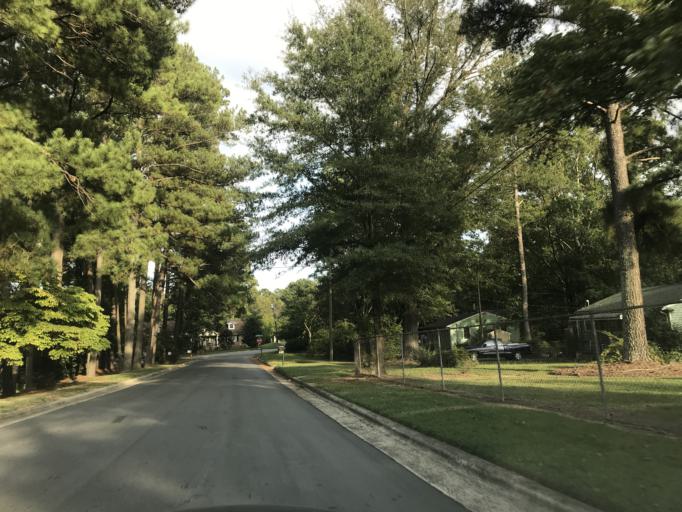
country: US
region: North Carolina
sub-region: Wake County
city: Raleigh
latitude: 35.7511
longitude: -78.6156
